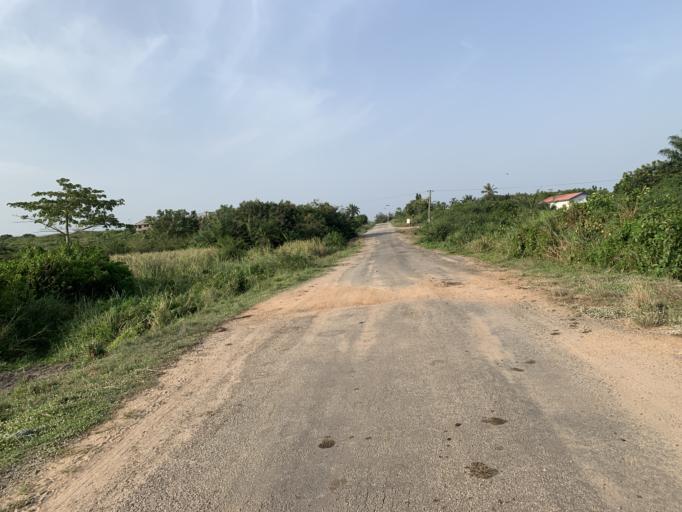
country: GH
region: Central
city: Winneba
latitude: 5.3891
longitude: -0.6029
